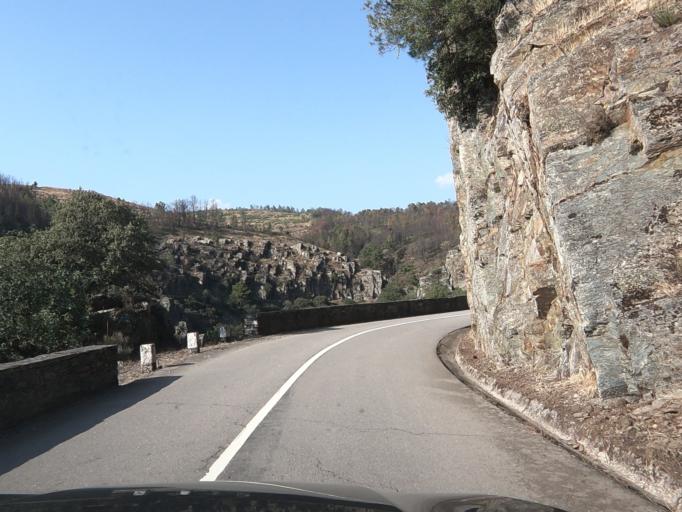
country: PT
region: Vila Real
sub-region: Sabrosa
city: Vilela
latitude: 41.2118
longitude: -7.6166
